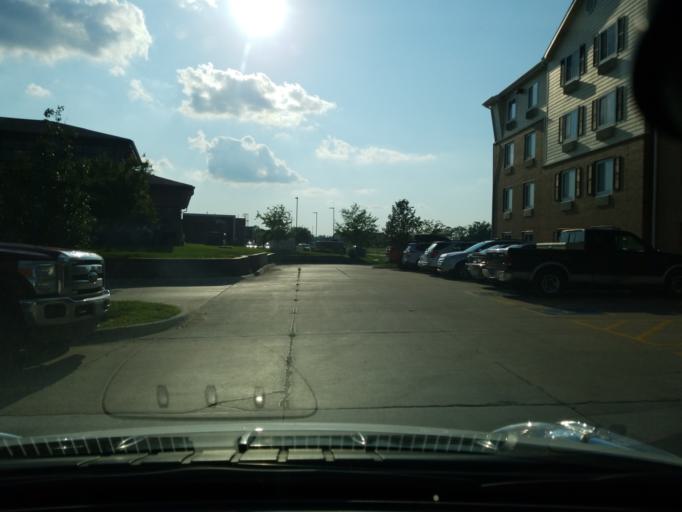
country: US
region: Nebraska
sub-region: Sarpy County
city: Offutt Air Force Base
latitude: 41.1384
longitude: -95.9536
